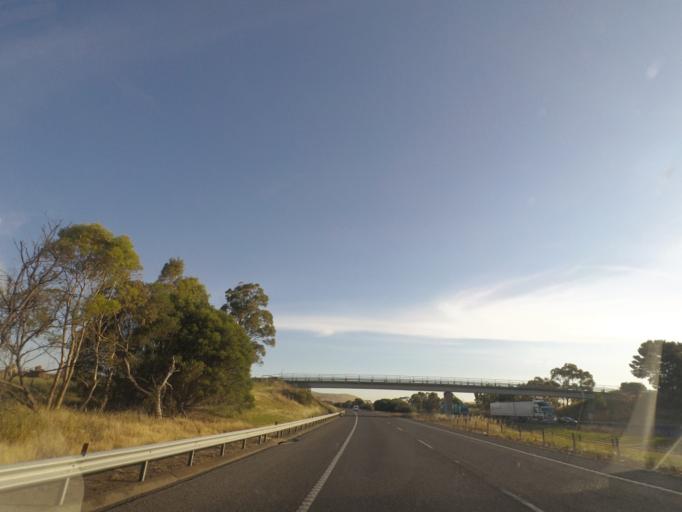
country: AU
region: Victoria
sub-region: Whittlesea
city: Whittlesea
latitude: -37.4344
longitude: 144.9822
